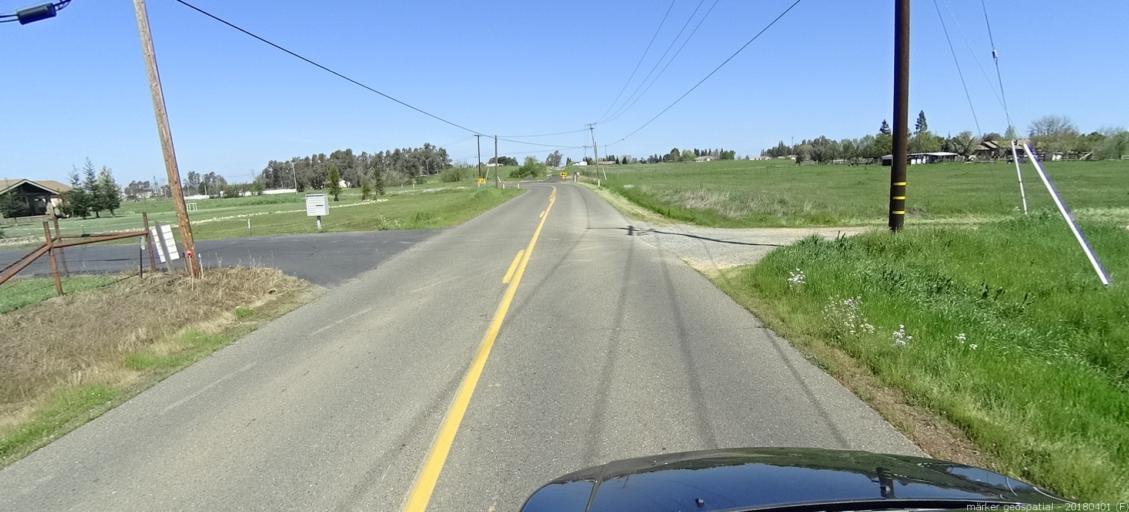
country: US
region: California
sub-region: Sacramento County
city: Wilton
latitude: 38.3976
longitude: -121.2422
